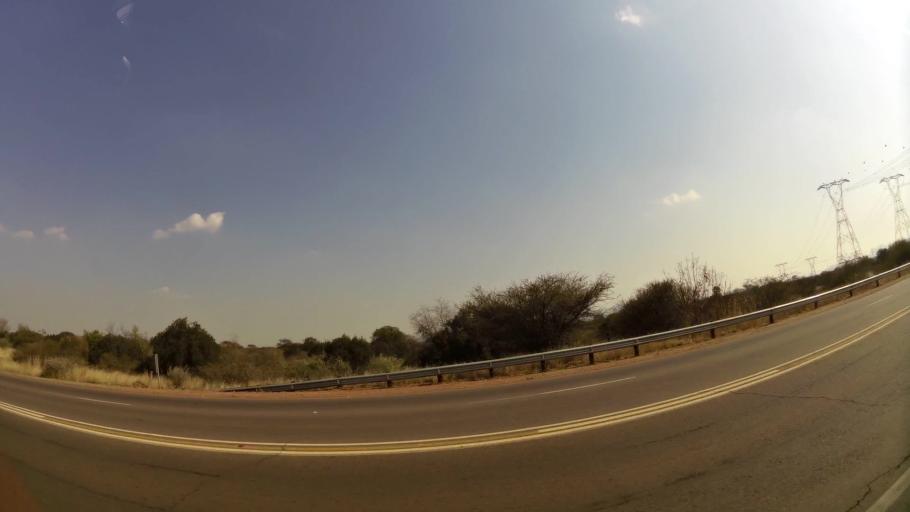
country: ZA
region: North-West
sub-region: Bojanala Platinum District Municipality
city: Mogwase
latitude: -25.3941
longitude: 27.0713
